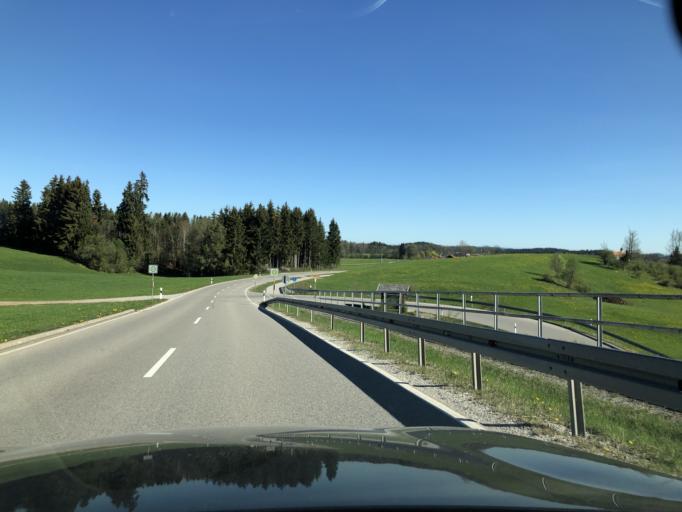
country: DE
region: Bavaria
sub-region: Swabia
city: Ruckholz
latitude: 47.6491
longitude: 10.5367
